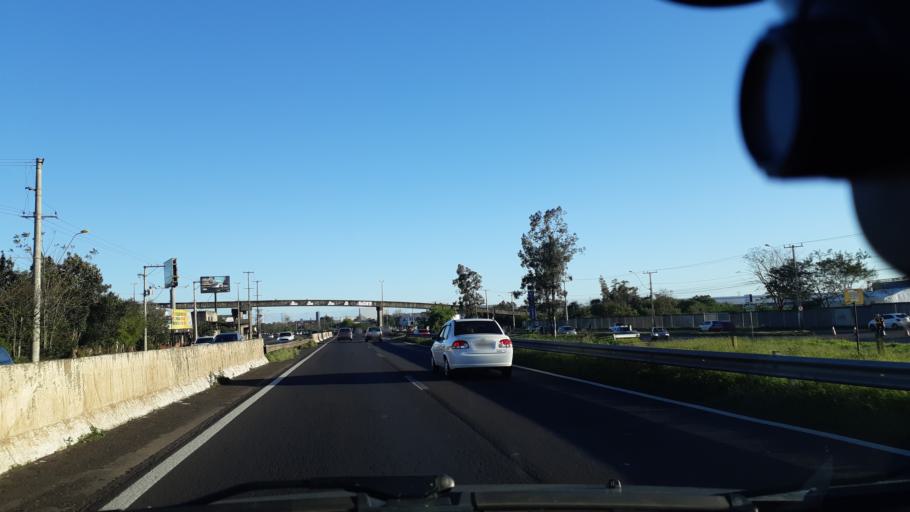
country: BR
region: Rio Grande do Sul
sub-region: Esteio
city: Esteio
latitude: -29.8578
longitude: -51.1807
